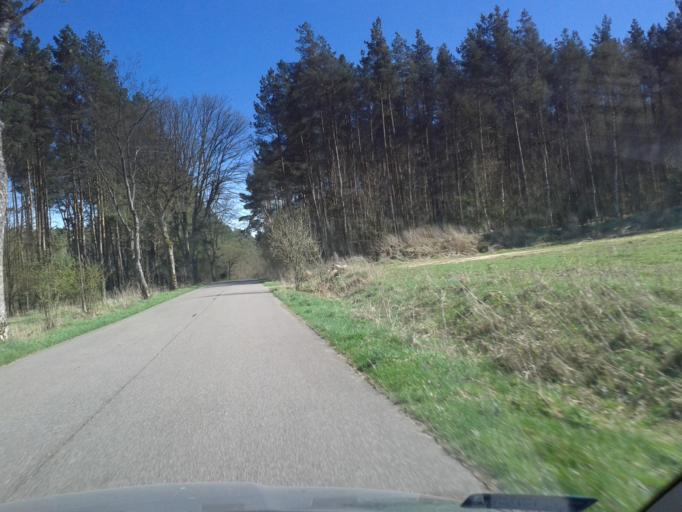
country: PL
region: West Pomeranian Voivodeship
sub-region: Powiat szczecinecki
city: Lubowo
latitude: 53.6397
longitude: 16.3270
